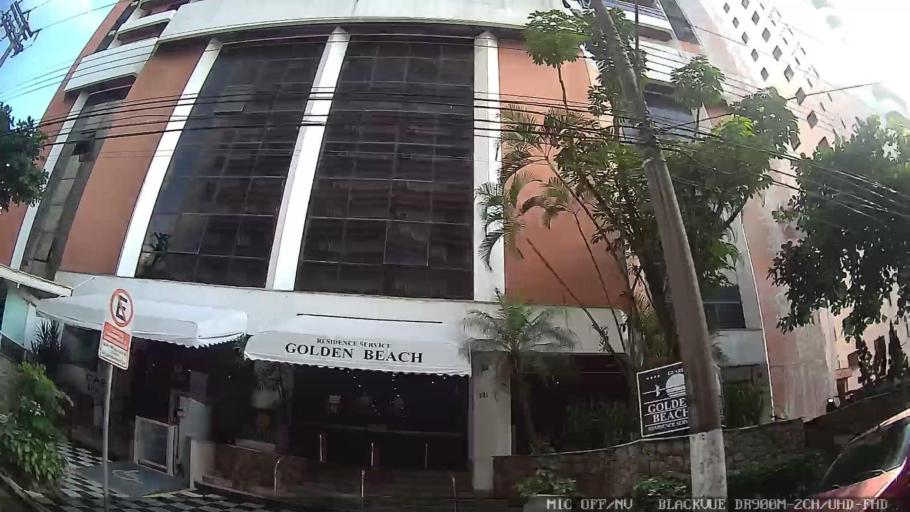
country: BR
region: Sao Paulo
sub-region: Guaruja
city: Guaruja
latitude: -23.9960
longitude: -46.2576
